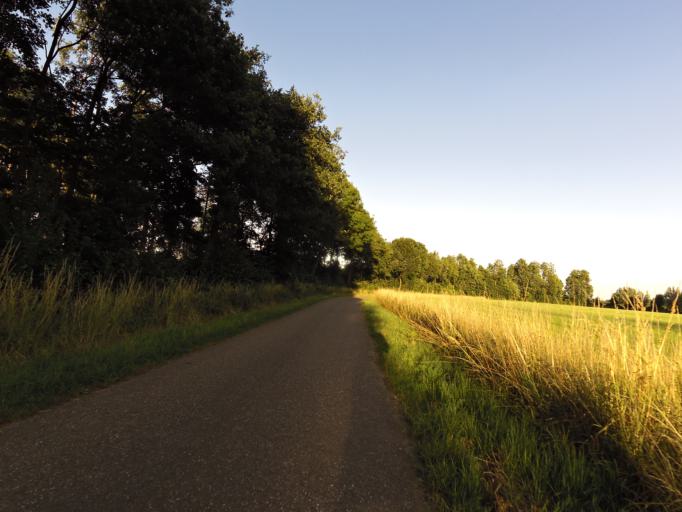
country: NL
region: Gelderland
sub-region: Gemeente Doesburg
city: Doesburg
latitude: 51.9940
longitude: 6.2020
